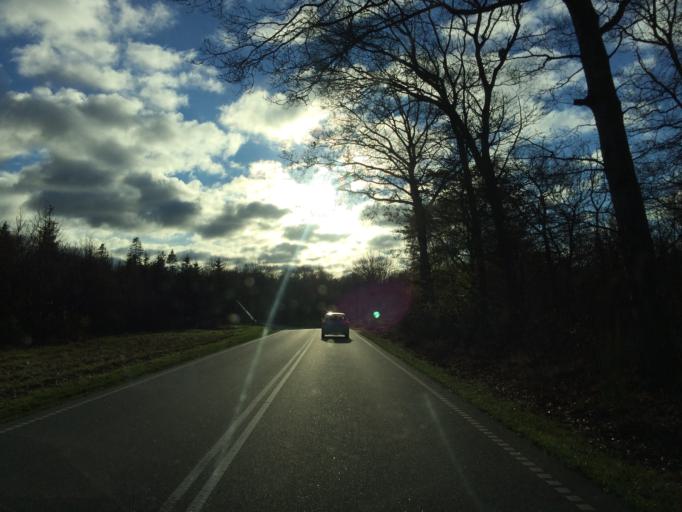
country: DK
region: Central Jutland
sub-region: Herning Kommune
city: Kibaek
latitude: 55.9510
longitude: 8.8858
